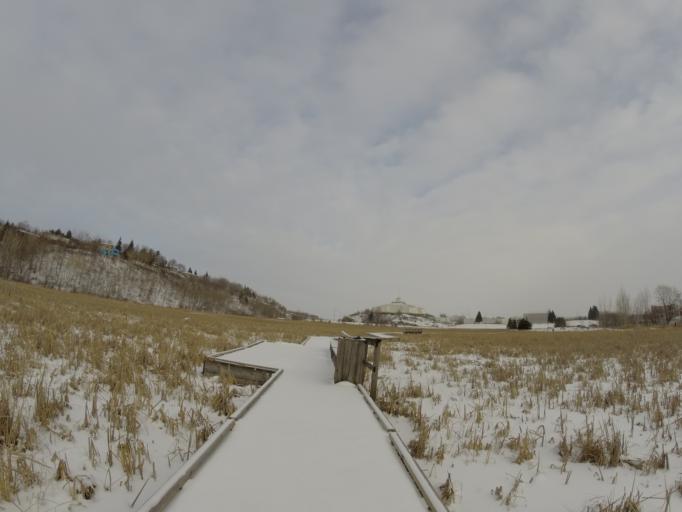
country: CA
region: Ontario
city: Greater Sudbury
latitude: 46.4711
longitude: -81.0003
